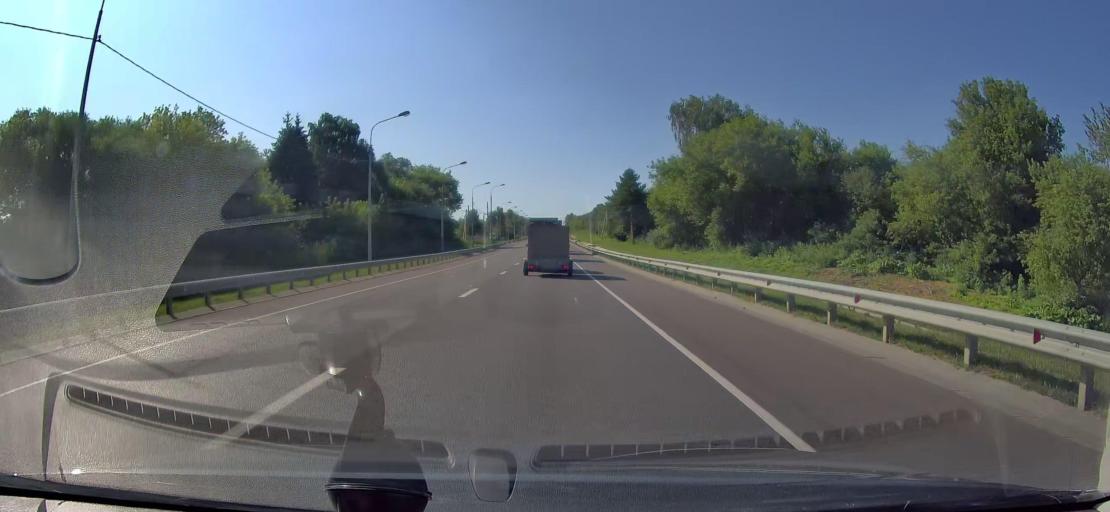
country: RU
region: Orjol
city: Kromy
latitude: 52.6212
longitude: 35.7590
